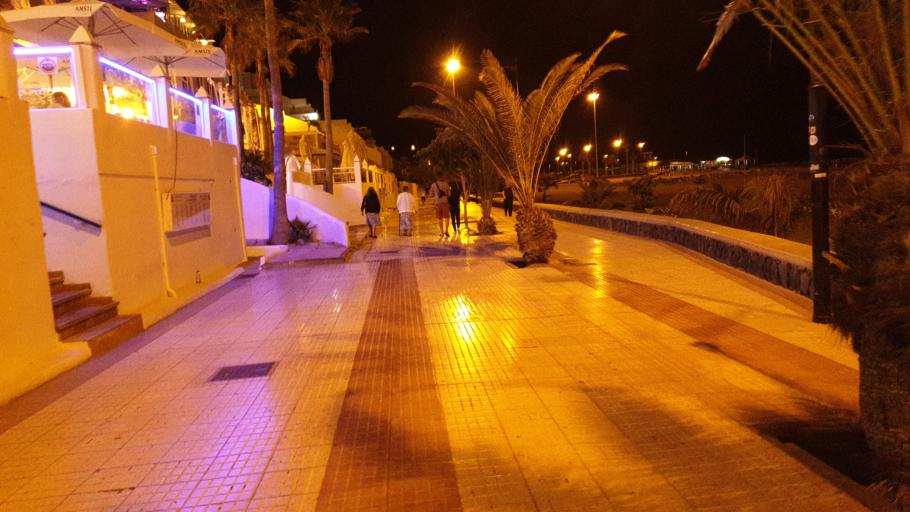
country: ES
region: Canary Islands
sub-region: Provincia de Santa Cruz de Tenerife
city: Playa de las Americas
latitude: 28.0517
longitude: -16.7224
